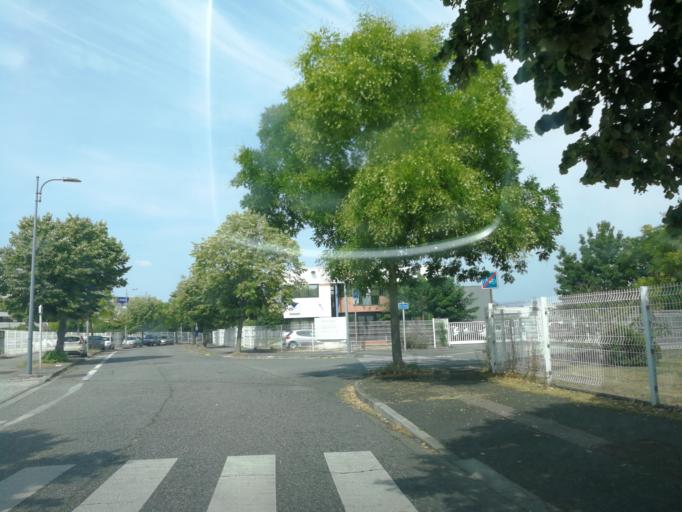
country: FR
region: Midi-Pyrenees
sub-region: Departement de la Haute-Garonne
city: Blagnac
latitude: 43.6402
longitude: 1.3703
